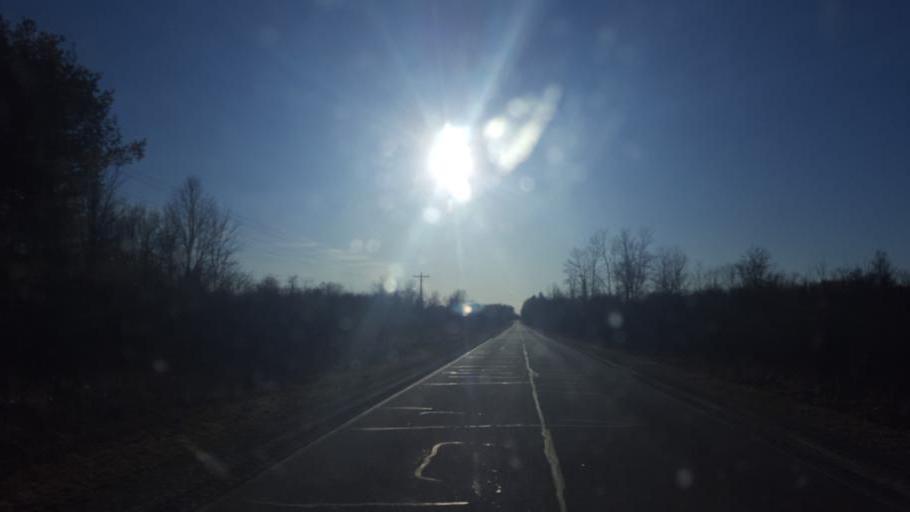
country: US
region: Michigan
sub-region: Mecosta County
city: Canadian Lakes
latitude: 43.5399
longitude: -85.2655
